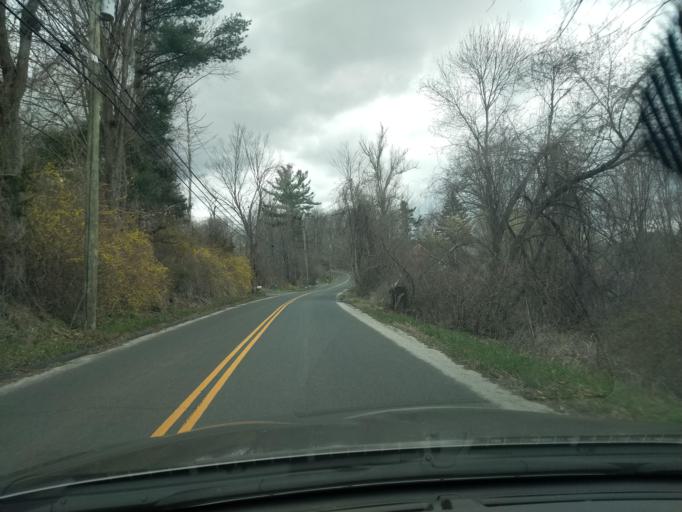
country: US
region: Connecticut
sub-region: Fairfield County
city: Newtown
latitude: 41.3615
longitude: -73.2836
